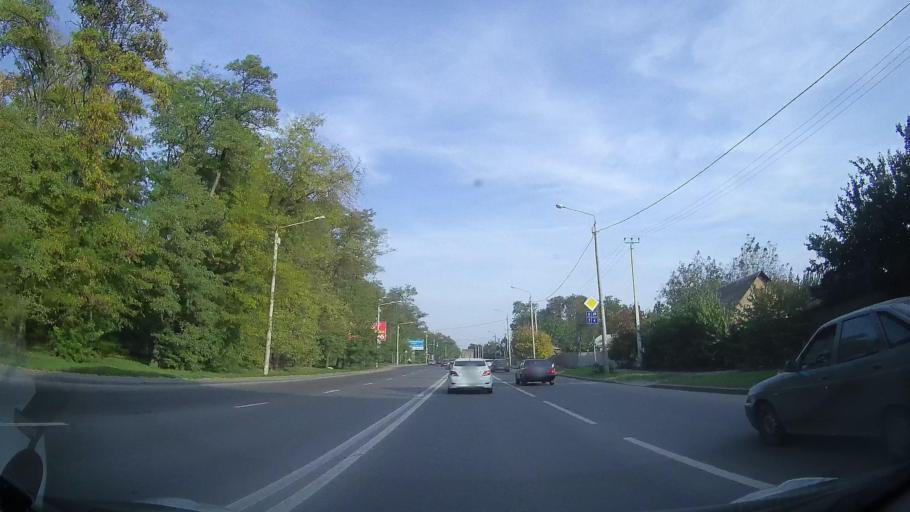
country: RU
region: Rostov
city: Imeni Chkalova
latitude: 47.2752
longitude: 39.7913
